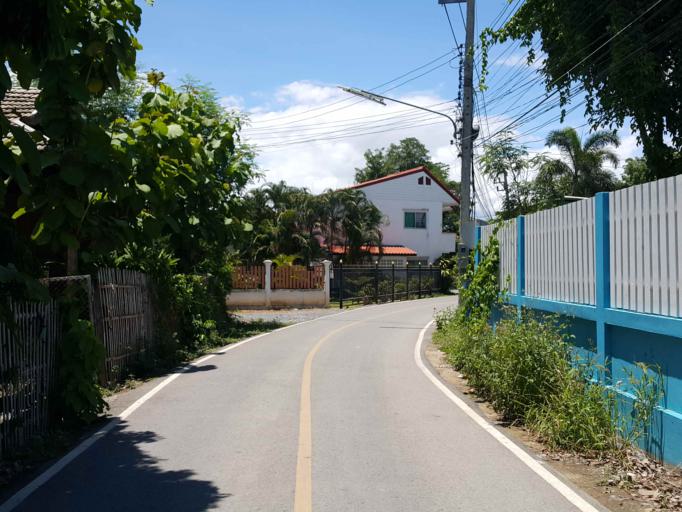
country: TH
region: Chiang Mai
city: Chiang Mai
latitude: 18.7474
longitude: 98.9984
